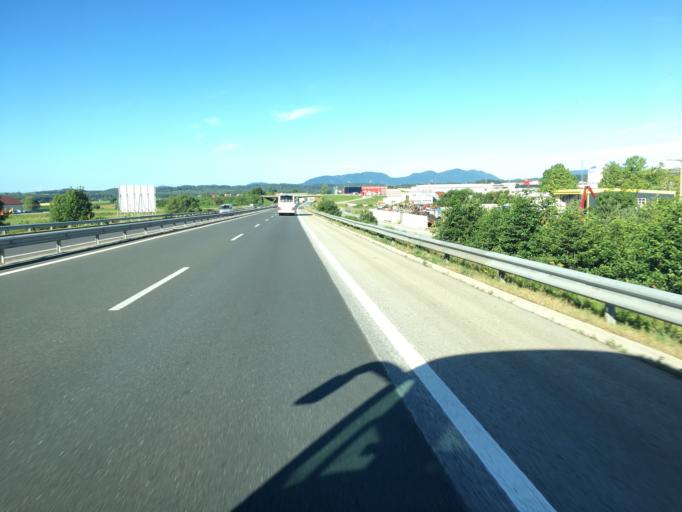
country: SI
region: Slovenska Bistrica
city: Slovenska Bistrica
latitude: 46.3894
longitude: 15.5872
